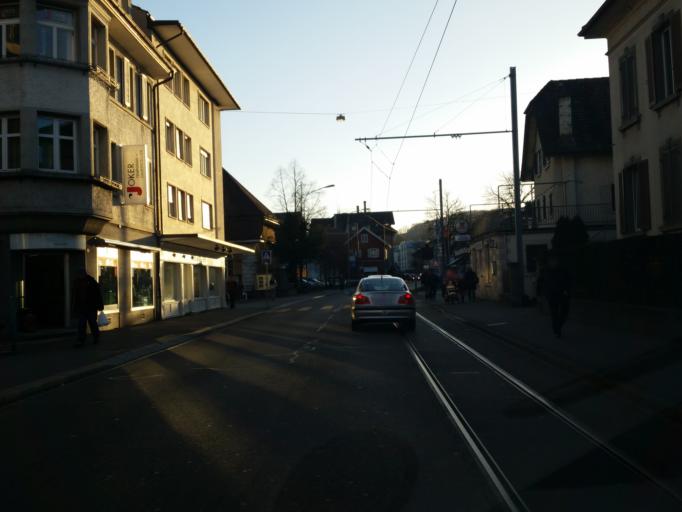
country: CH
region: Zurich
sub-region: Bezirk Dietikon
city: Dietikon
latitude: 47.4039
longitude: 8.4023
